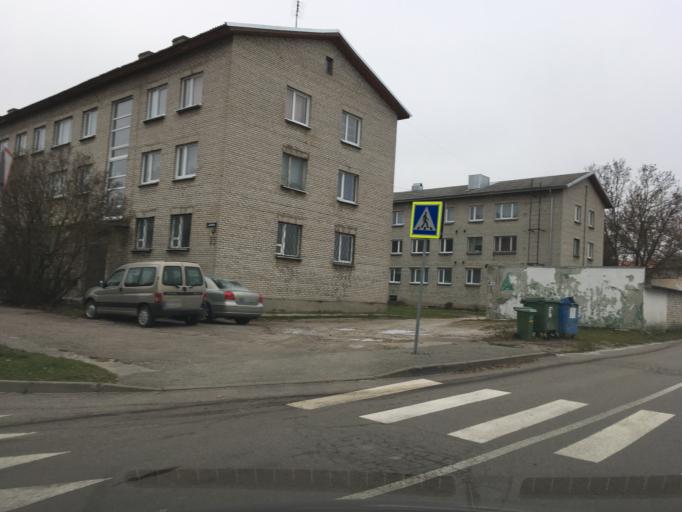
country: EE
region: Ida-Virumaa
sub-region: Johvi vald
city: Johvi
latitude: 59.3625
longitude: 27.4099
